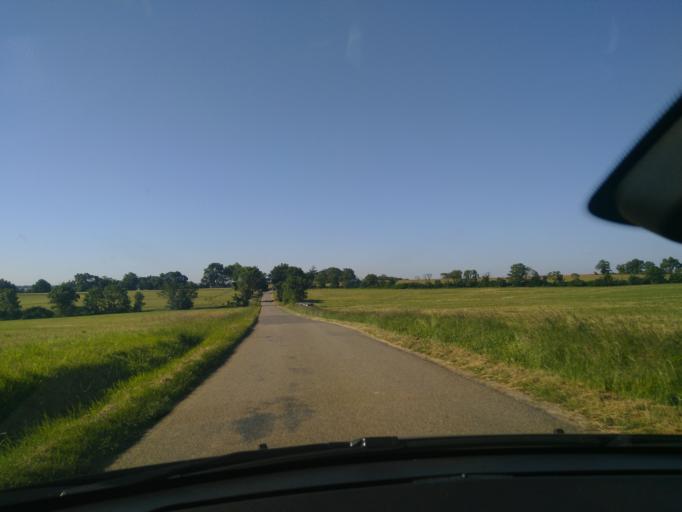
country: FR
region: Midi-Pyrenees
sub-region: Departement du Tarn-et-Garonne
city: Beaumont-de-Lomagne
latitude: 43.7602
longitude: 0.9207
